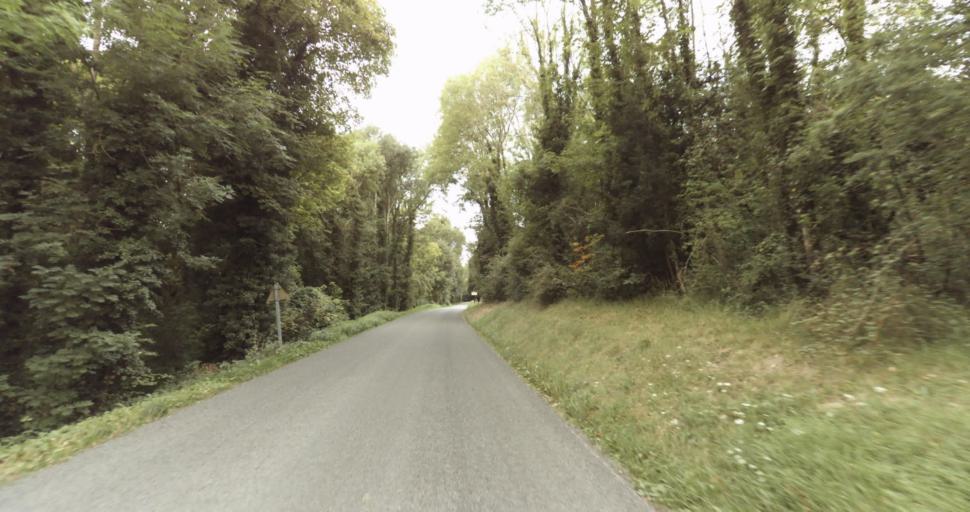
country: FR
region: Centre
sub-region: Departement d'Eure-et-Loir
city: Vert-en-Drouais
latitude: 48.7651
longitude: 1.3123
